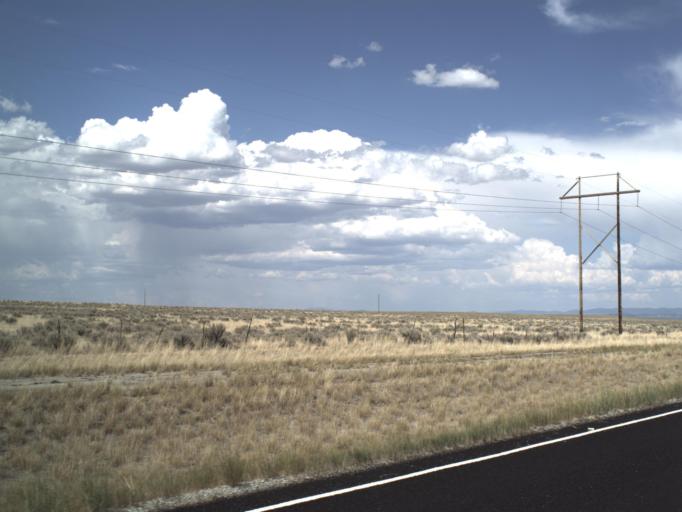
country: US
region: Idaho
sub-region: Power County
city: American Falls
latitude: 41.9666
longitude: -113.0750
